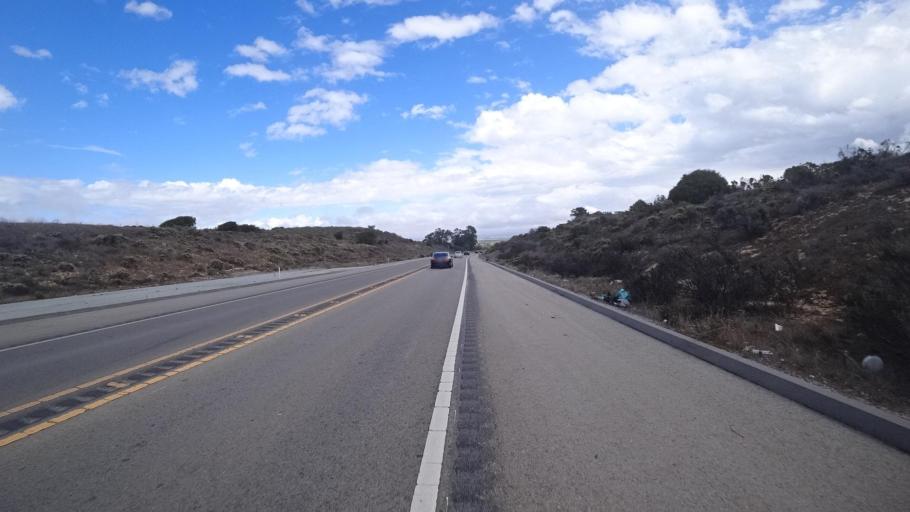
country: US
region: California
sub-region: Monterey County
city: Marina
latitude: 36.6733
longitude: -121.7519
